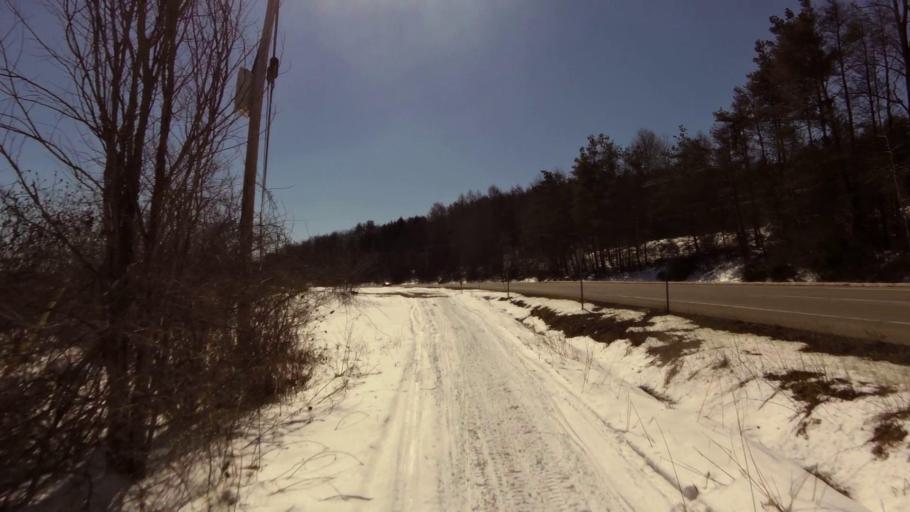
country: US
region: New York
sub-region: Allegany County
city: Houghton
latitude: 42.3806
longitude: -78.1548
